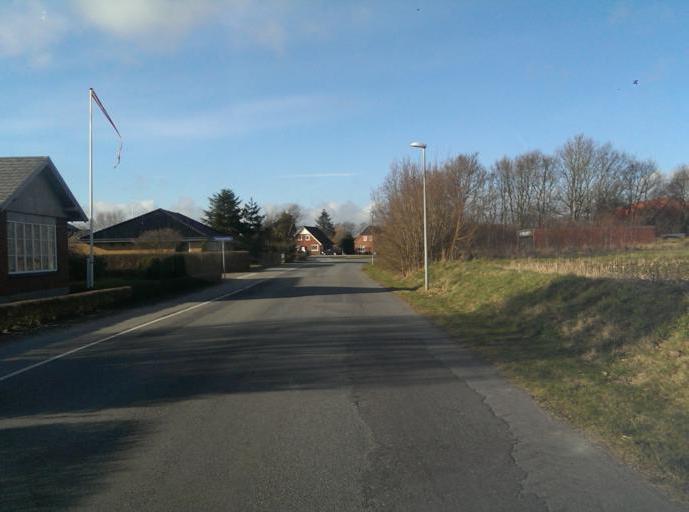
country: DK
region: South Denmark
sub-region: Esbjerg Kommune
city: Bramming
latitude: 55.4268
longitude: 8.6470
